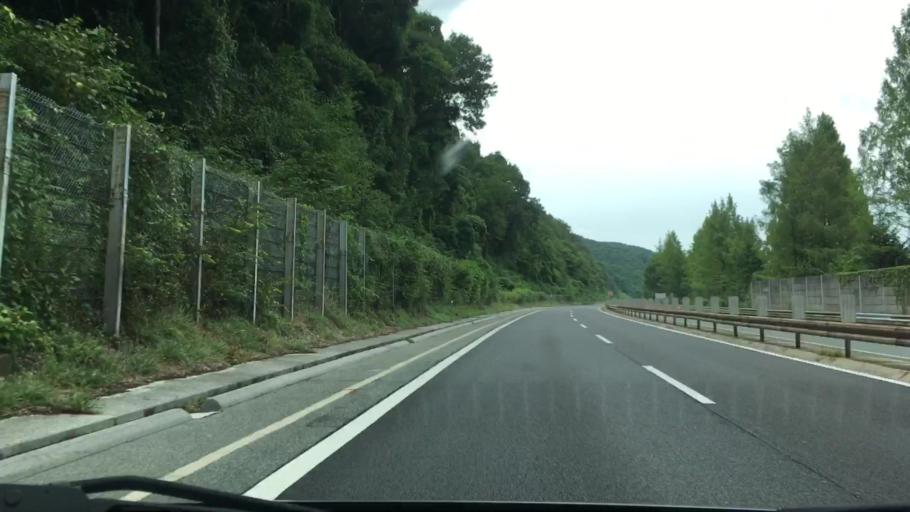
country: JP
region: Okayama
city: Niimi
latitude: 34.9734
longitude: 133.6223
